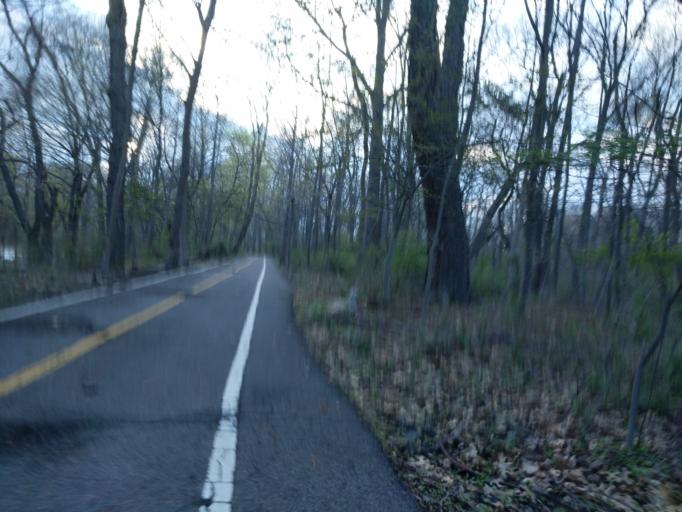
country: US
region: New York
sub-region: Westchester County
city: Pelham Manor
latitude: 40.8637
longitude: -73.8100
